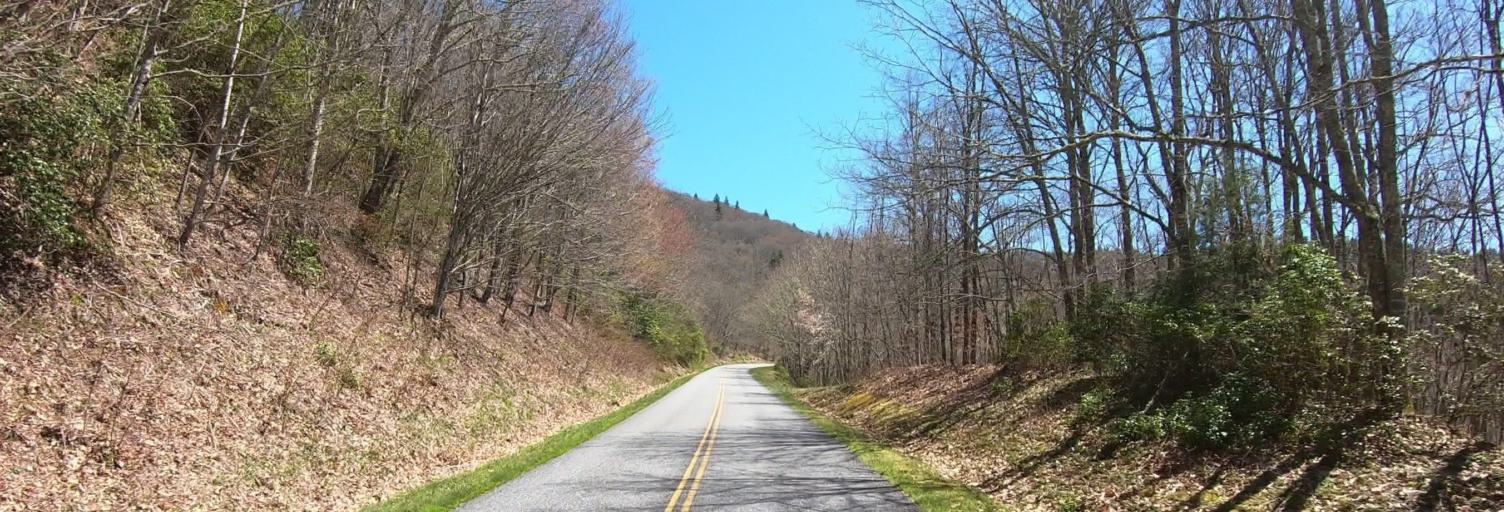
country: US
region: North Carolina
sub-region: Haywood County
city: Maggie Valley
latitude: 35.4786
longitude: -83.1473
